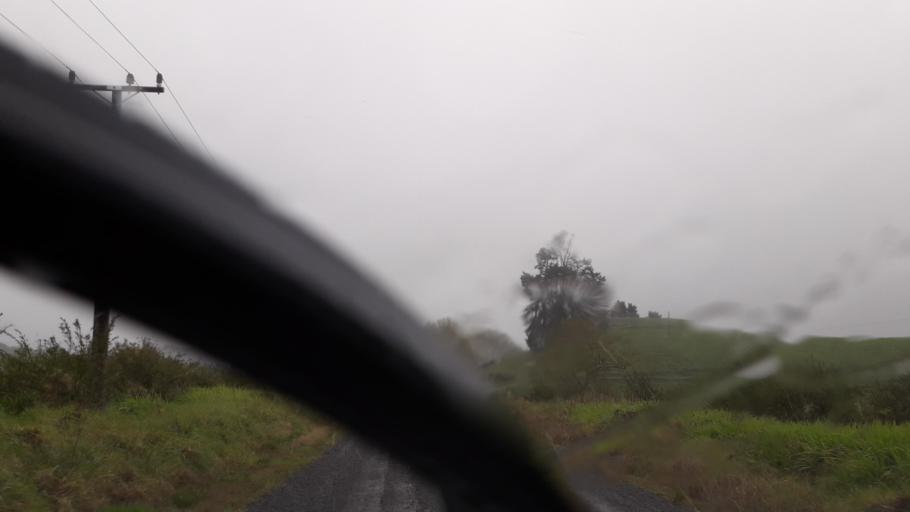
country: NZ
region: Northland
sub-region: Far North District
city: Waimate North
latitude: -35.4841
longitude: 173.6996
